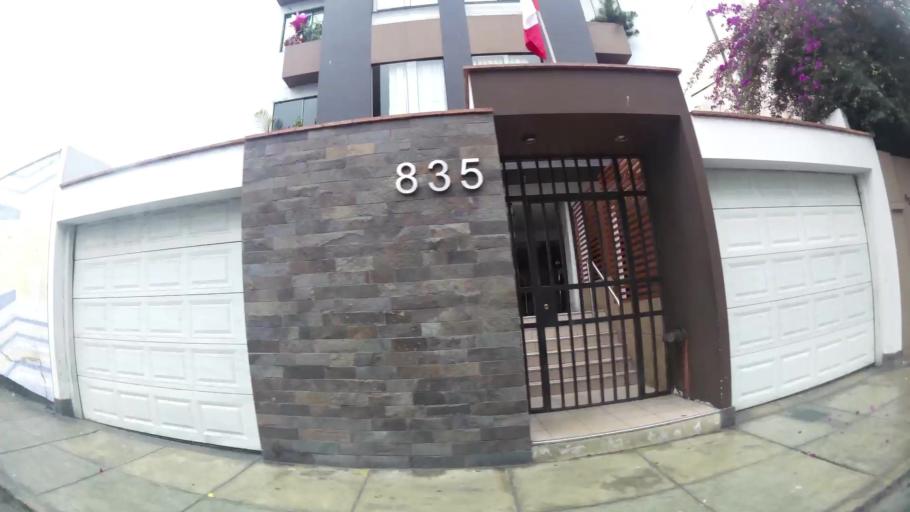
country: PE
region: Lima
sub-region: Lima
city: San Isidro
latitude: -12.1213
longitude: -77.0385
